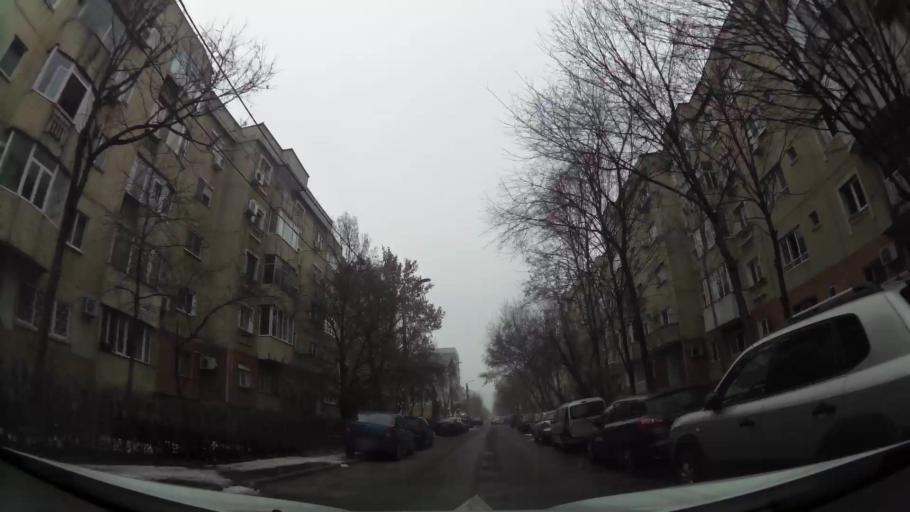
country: RO
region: Ilfov
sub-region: Comuna Chiajna
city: Rosu
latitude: 44.4399
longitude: 26.0318
